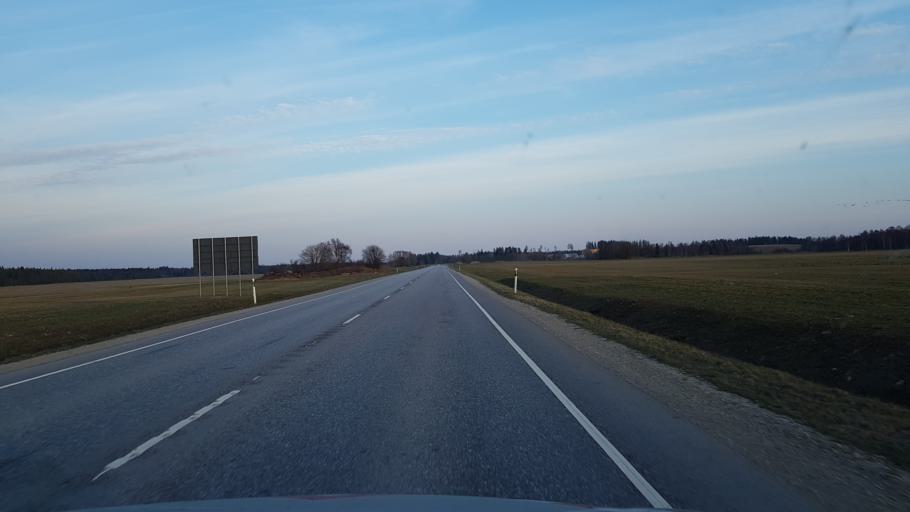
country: EE
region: Laeaene-Virumaa
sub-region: Someru vald
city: Someru
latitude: 59.3537
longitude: 26.3979
